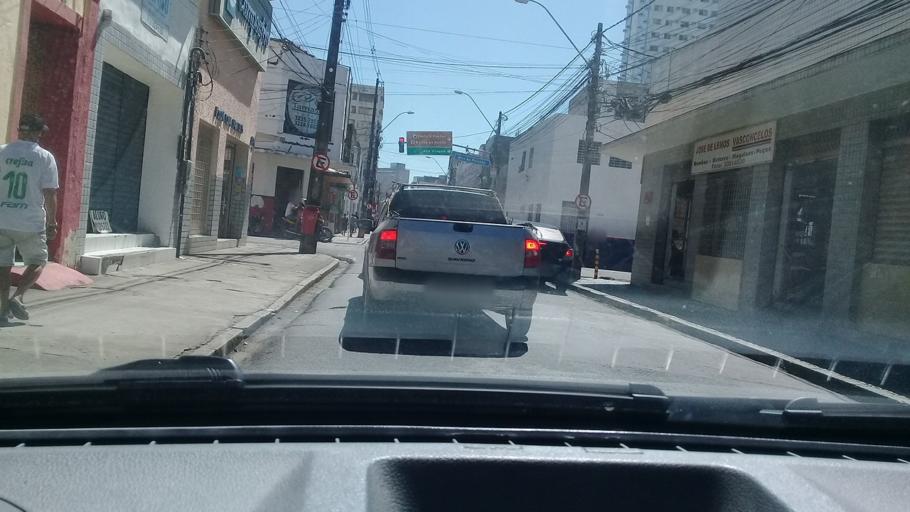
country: BR
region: Pernambuco
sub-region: Recife
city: Recife
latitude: -8.0712
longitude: -34.8840
